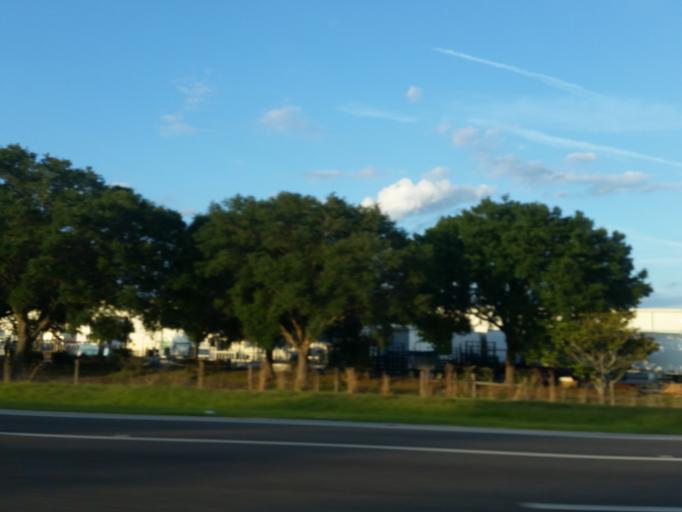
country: US
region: Florida
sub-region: Sarasota County
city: Nokomis
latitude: 27.1402
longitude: -82.4095
